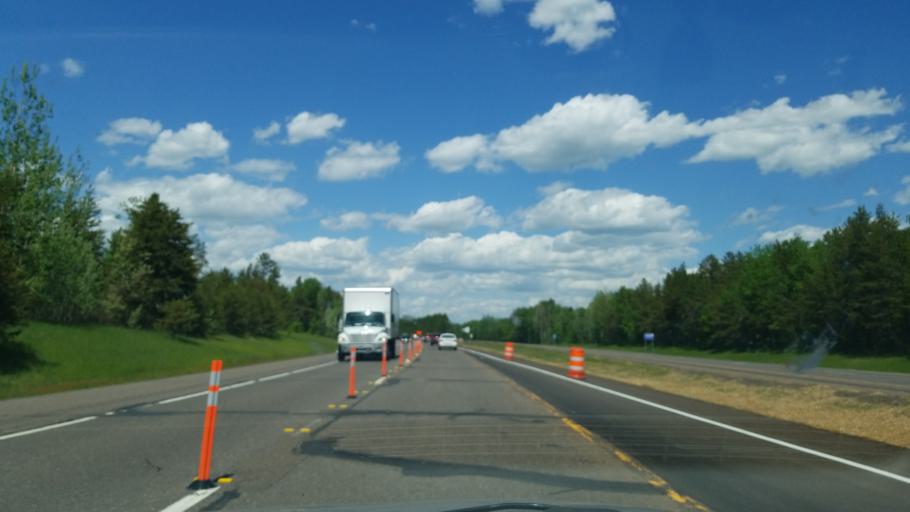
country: US
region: Minnesota
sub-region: Carlton County
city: Moose Lake
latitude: 46.3793
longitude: -92.7863
